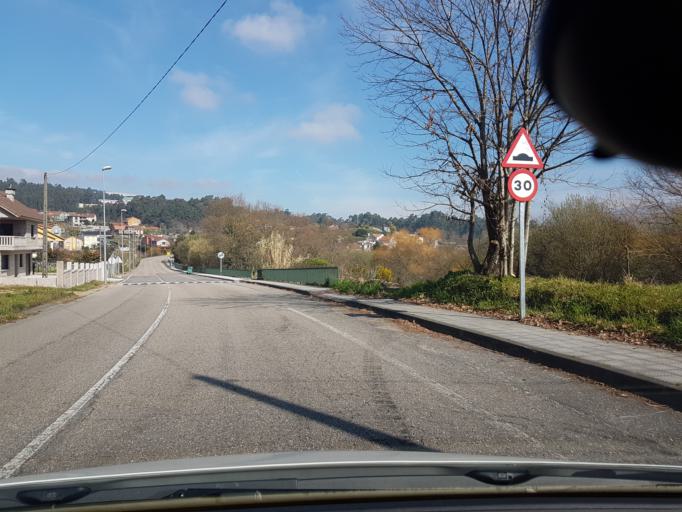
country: ES
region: Galicia
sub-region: Provincia de Pontevedra
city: Porrino
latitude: 42.1978
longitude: -8.6490
